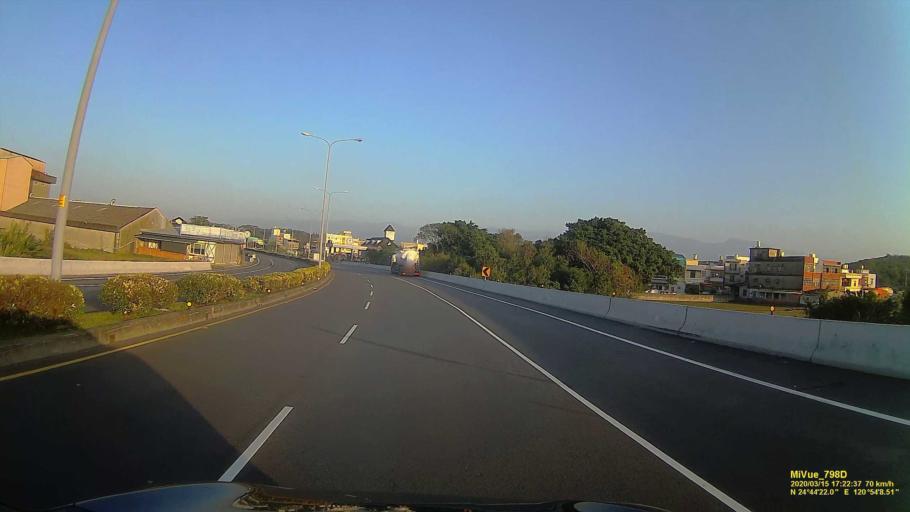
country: TW
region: Taiwan
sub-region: Hsinchu
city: Hsinchu
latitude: 24.7392
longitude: 120.9027
